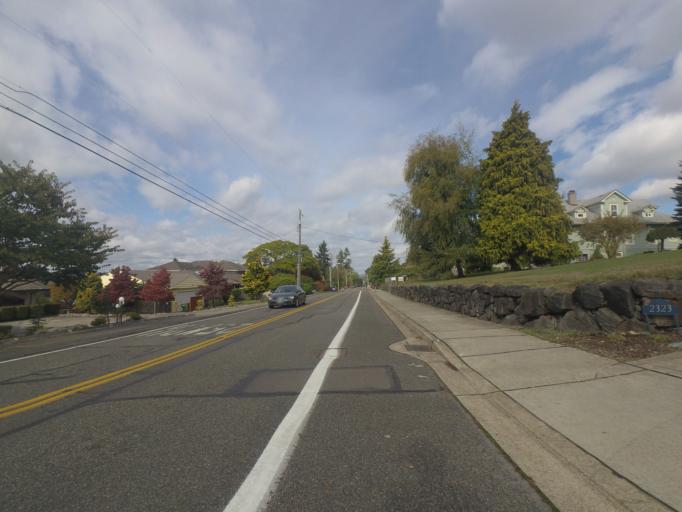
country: US
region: Washington
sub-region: Pierce County
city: University Place
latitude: 47.2381
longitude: -122.5449
